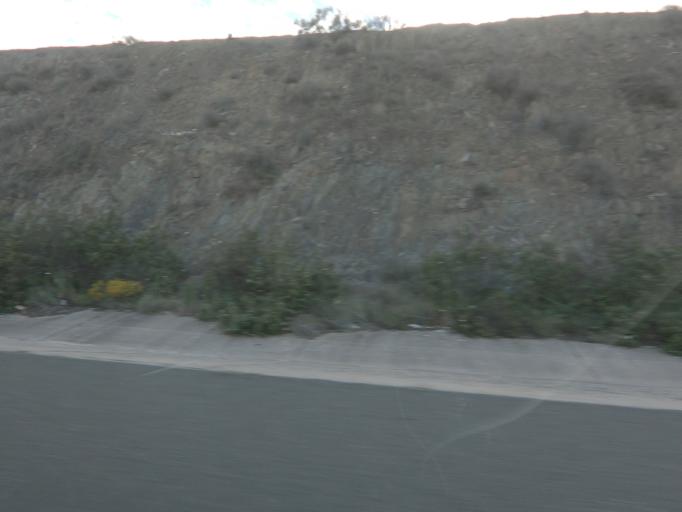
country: ES
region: Extremadura
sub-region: Provincia de Caceres
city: Hinojal
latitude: 39.7314
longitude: -6.4120
